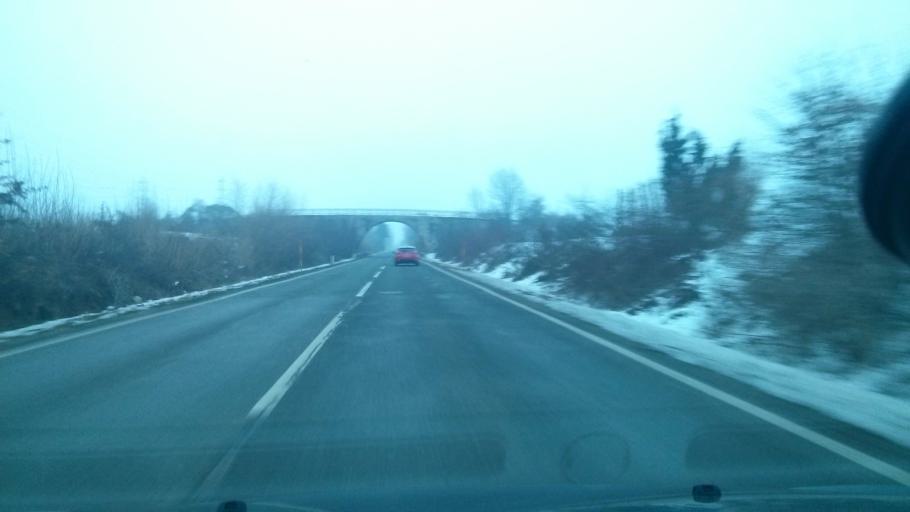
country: SI
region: Dol pri Ljubljani
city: Dol pri Ljubljani
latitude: 46.0908
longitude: 14.5989
